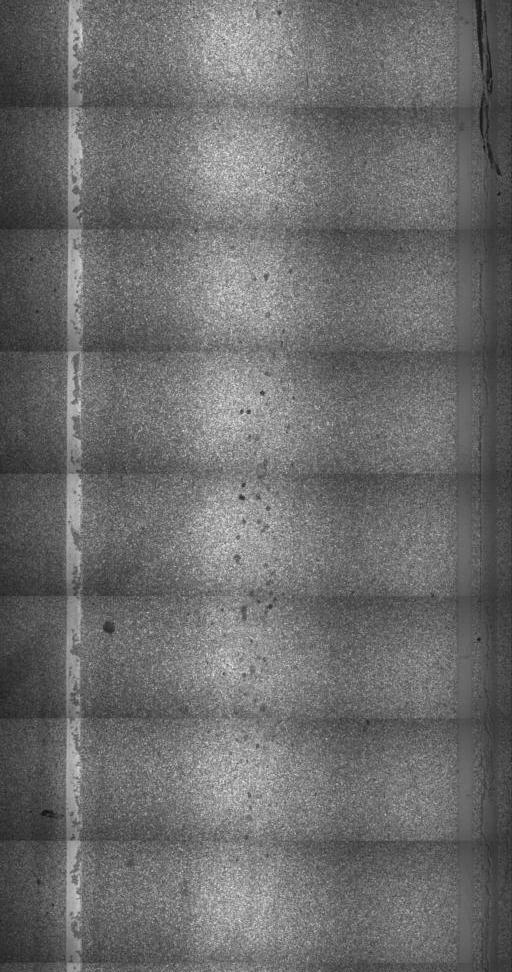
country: US
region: Vermont
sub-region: Franklin County
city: Swanton
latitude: 44.8865
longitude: -73.0923
